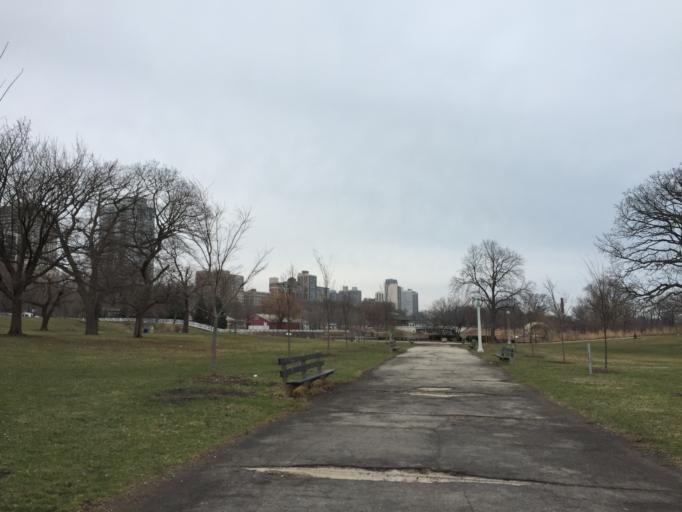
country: US
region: Illinois
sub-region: Cook County
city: Chicago
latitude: 41.9155
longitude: -87.6319
